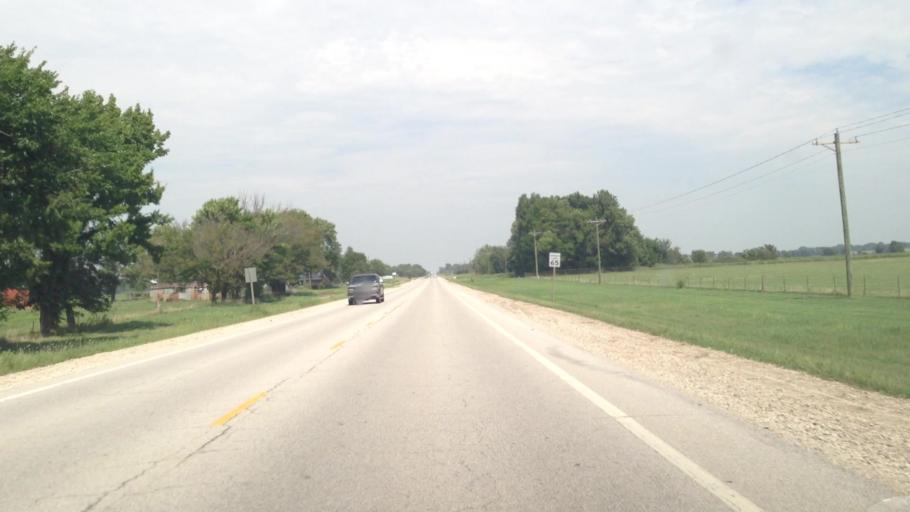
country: US
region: Kansas
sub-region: Neosho County
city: Erie
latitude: 37.5775
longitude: -95.2524
